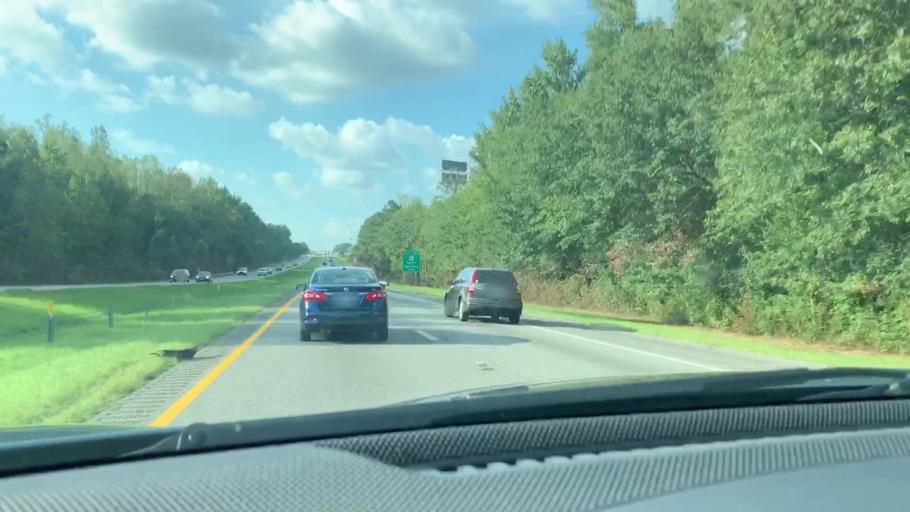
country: US
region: South Carolina
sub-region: Calhoun County
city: Saint Matthews
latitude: 33.6599
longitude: -80.8890
